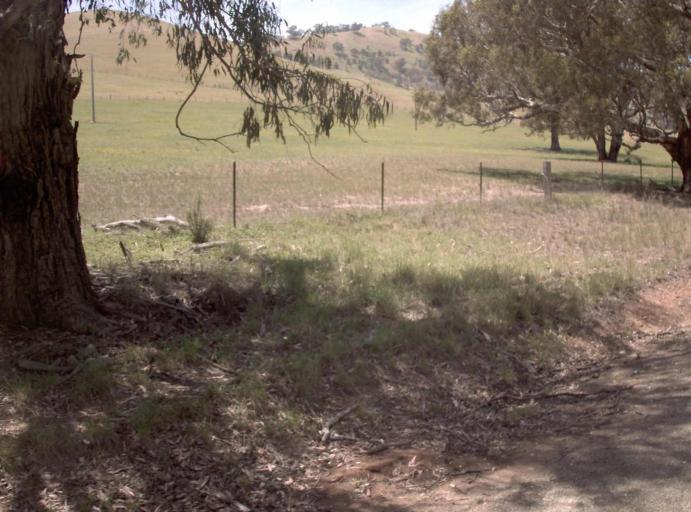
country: AU
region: Victoria
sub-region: East Gippsland
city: Bairnsdale
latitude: -37.3409
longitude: 147.7925
